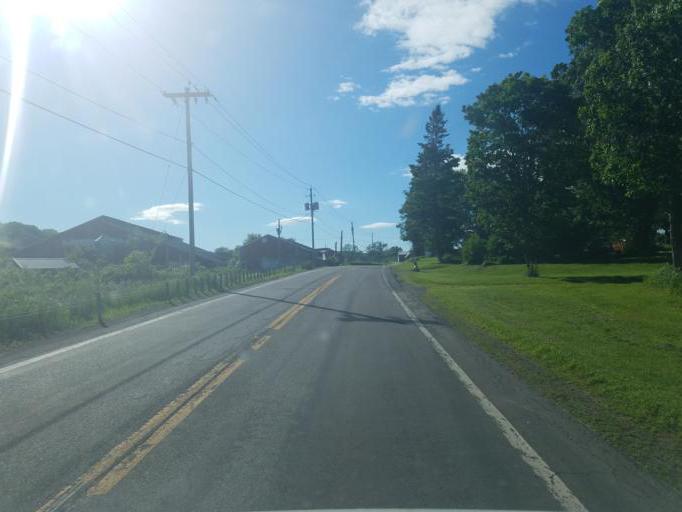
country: US
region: New York
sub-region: Herkimer County
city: Little Falls
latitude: 43.0101
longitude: -74.7971
